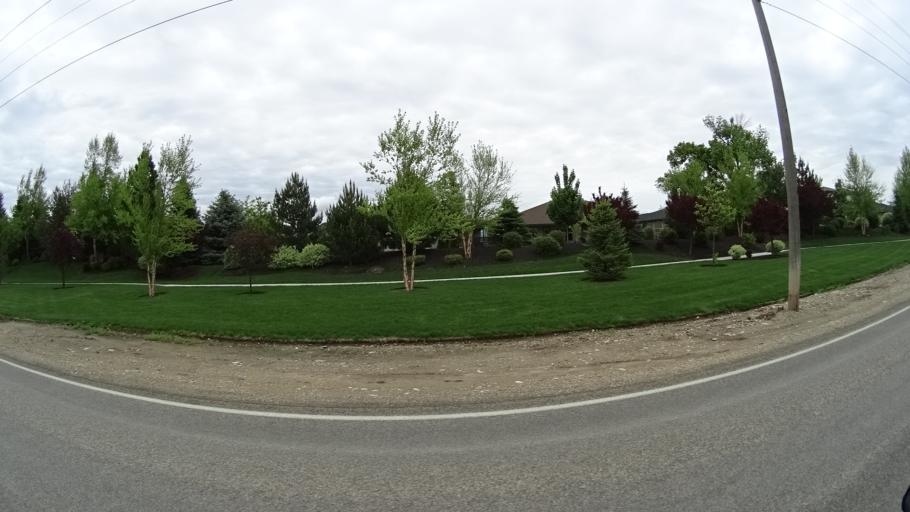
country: US
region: Idaho
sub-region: Ada County
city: Eagle
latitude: 43.7111
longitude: -116.4136
